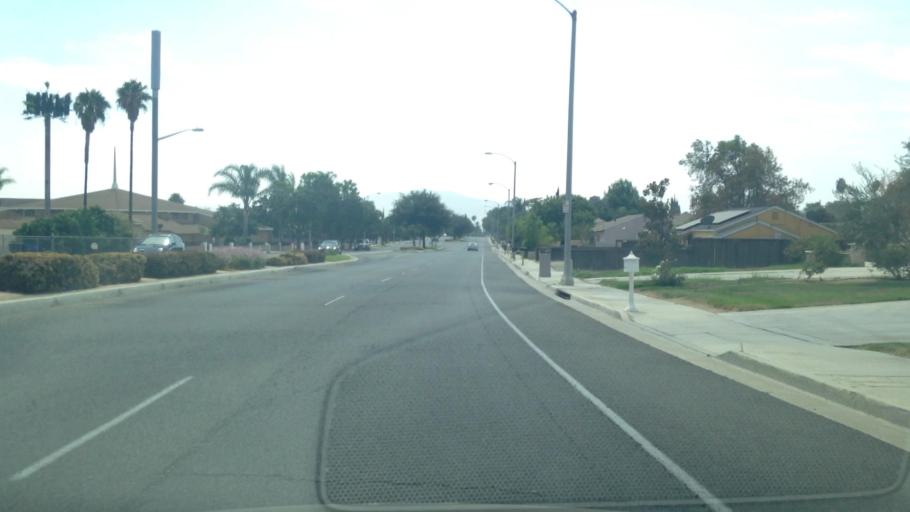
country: US
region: California
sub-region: Riverside County
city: Pedley
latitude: 33.9382
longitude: -117.4973
